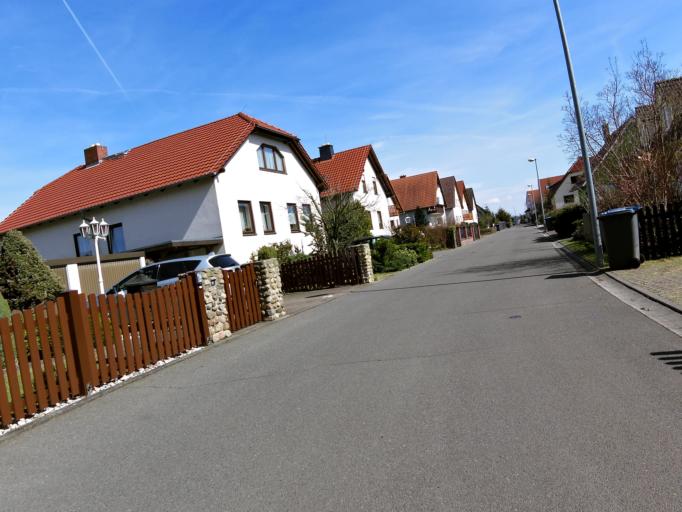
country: DE
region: Saxony
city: Borsdorf
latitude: 51.3408
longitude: 12.4915
